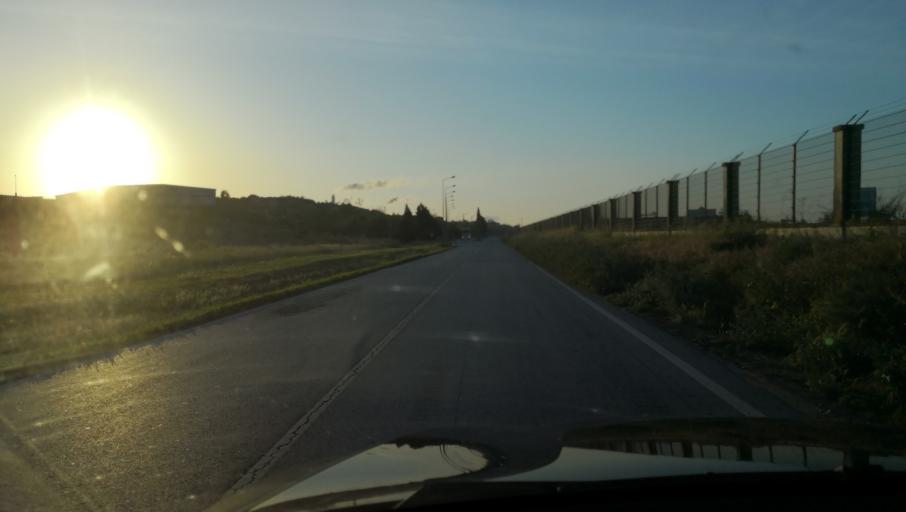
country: PT
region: Setubal
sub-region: Setubal
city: Setubal
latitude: 38.4937
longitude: -8.8307
